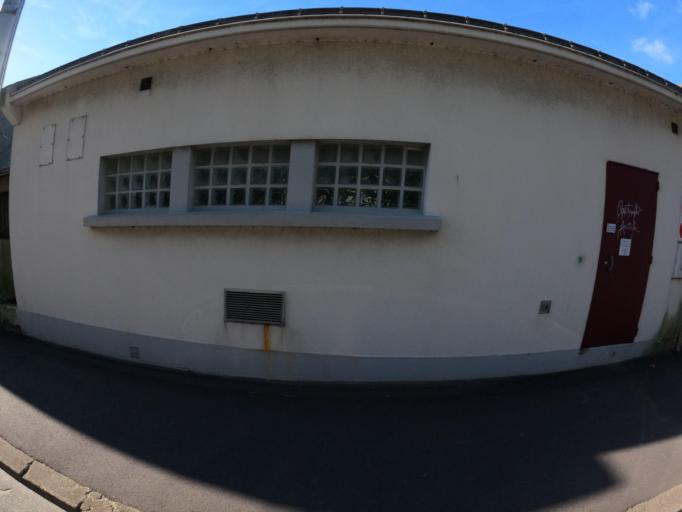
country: FR
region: Pays de la Loire
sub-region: Departement de la Loire-Atlantique
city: Le Croisic
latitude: 47.2907
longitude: -2.5080
